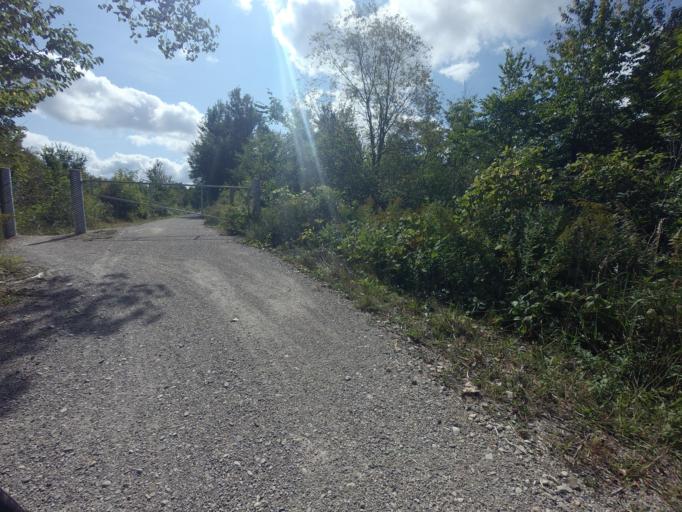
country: CA
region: Ontario
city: Huron East
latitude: 43.7074
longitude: -81.3656
